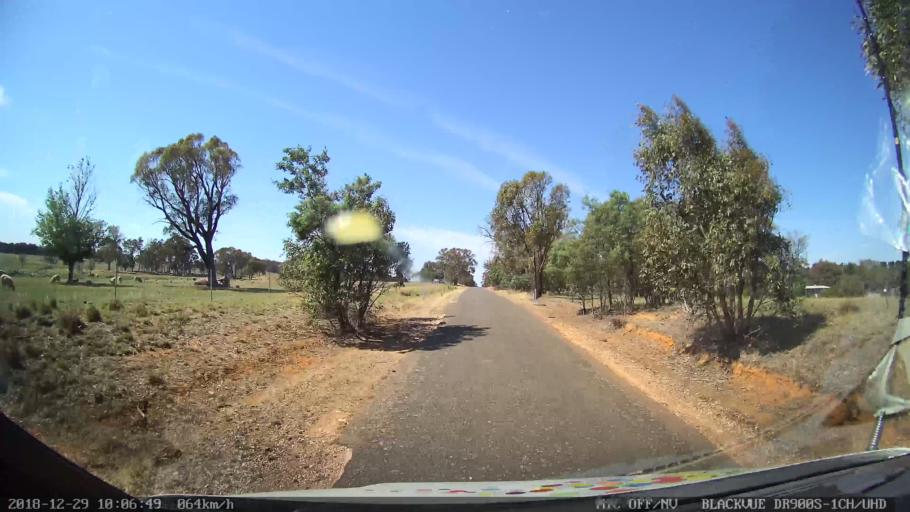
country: AU
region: New South Wales
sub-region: Yass Valley
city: Gundaroo
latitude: -34.8468
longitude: 149.4544
